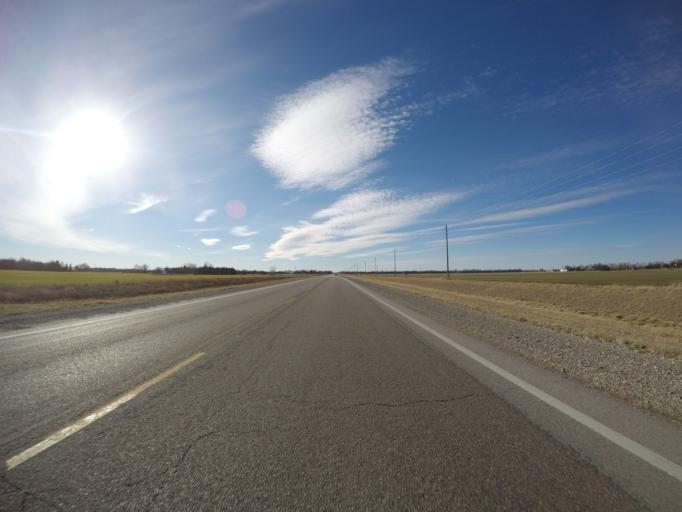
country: US
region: Kansas
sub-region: McPherson County
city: Moundridge
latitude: 38.3770
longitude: -97.4787
